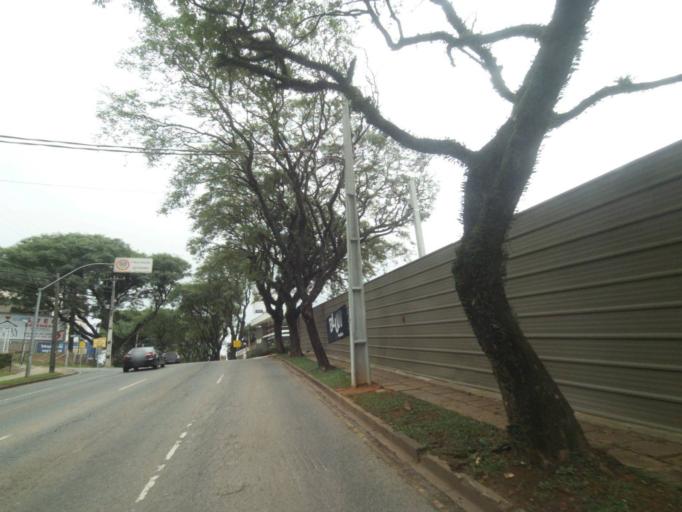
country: BR
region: Parana
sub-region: Curitiba
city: Curitiba
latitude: -25.4357
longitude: -49.3098
